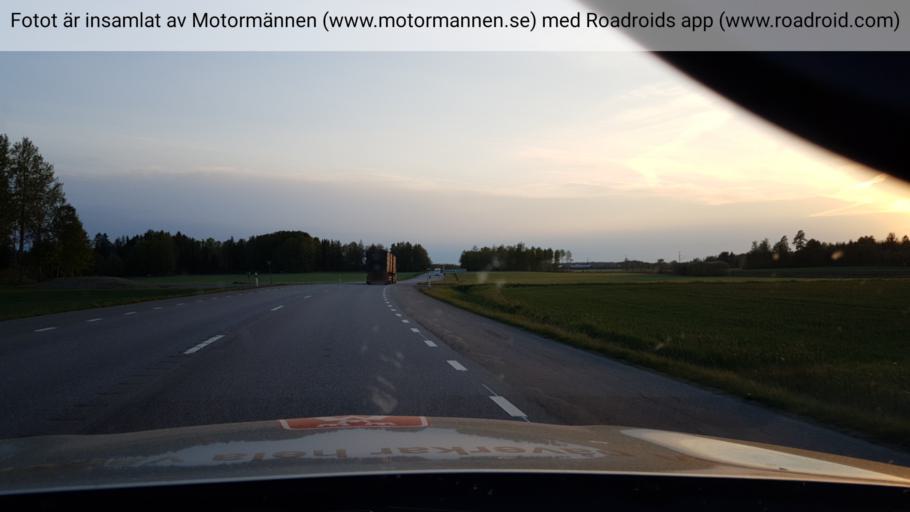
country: SE
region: Vaestmanland
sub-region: Sala Kommun
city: Sala
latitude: 59.9276
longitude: 16.7094
